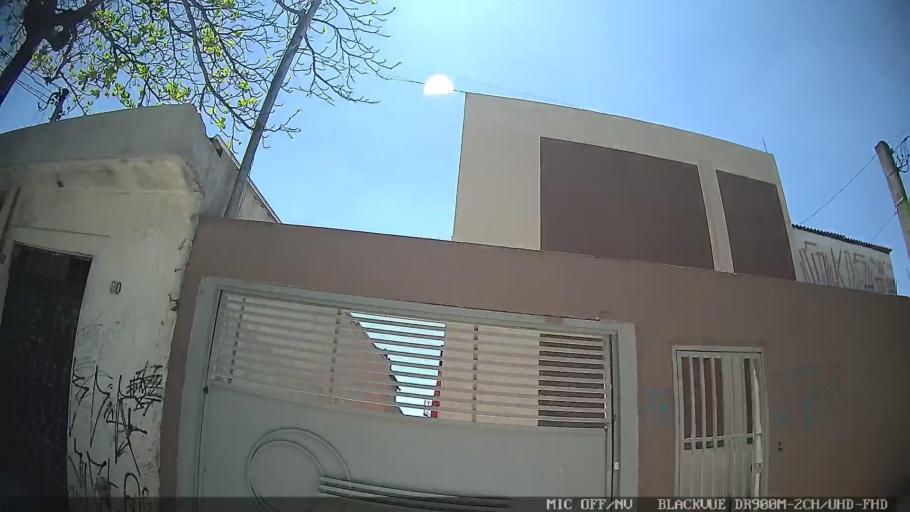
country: BR
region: Sao Paulo
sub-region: Sao Caetano Do Sul
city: Sao Caetano do Sul
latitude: -23.6021
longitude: -46.5575
